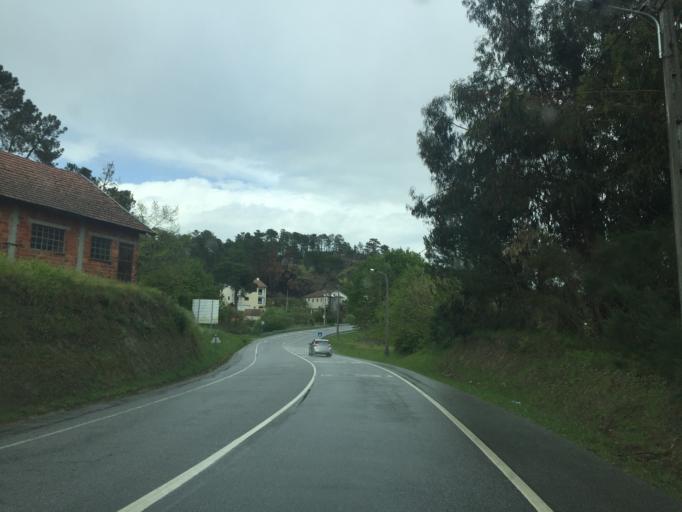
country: PT
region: Viseu
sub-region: Viseu
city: Abraveses
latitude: 40.6689
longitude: -7.9876
